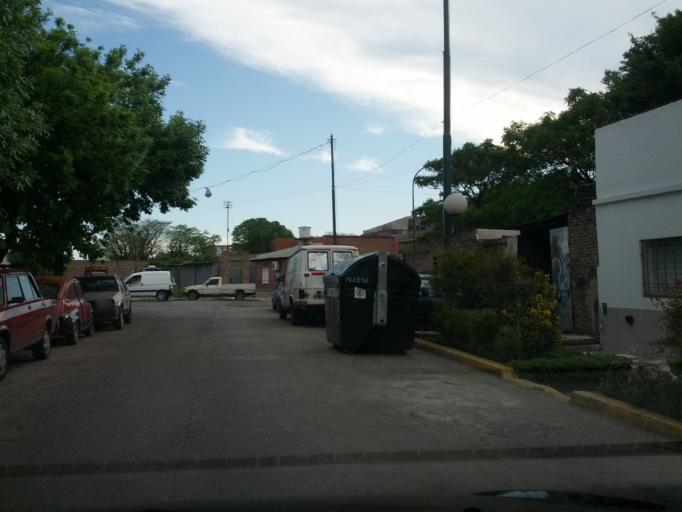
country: AR
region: Buenos Aires F.D.
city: Villa Lugano
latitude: -34.6528
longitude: -58.4294
